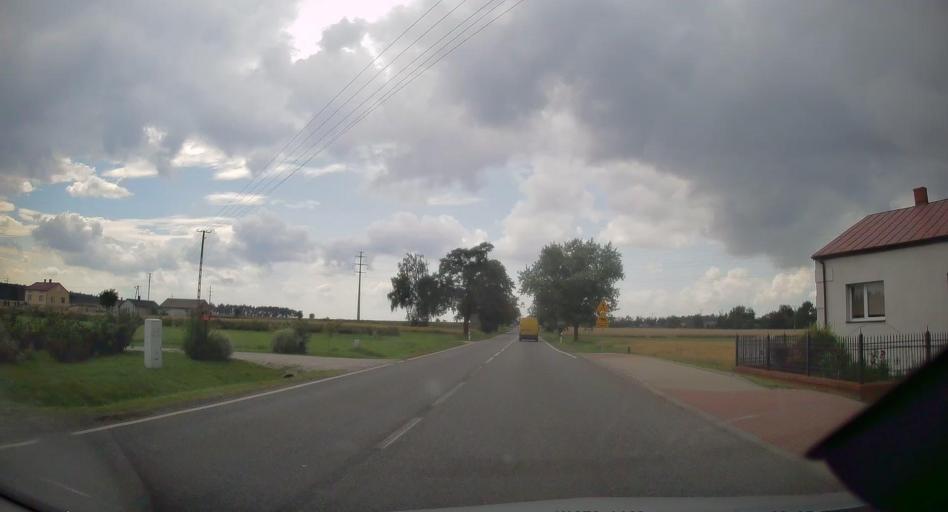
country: PL
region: Lodz Voivodeship
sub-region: Powiat skierniewicki
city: Gluchow
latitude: 51.7754
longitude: 20.1235
